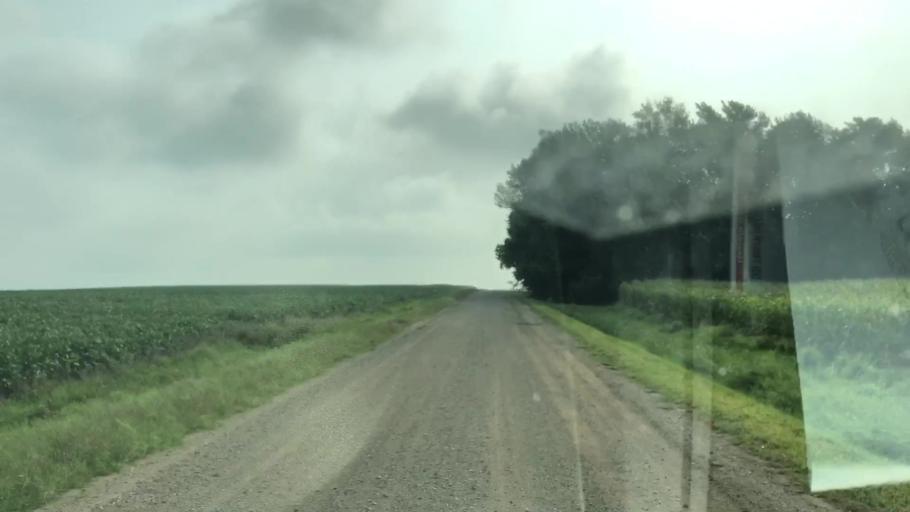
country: US
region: Iowa
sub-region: Sioux County
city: Hull
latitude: 43.2298
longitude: -96.0602
